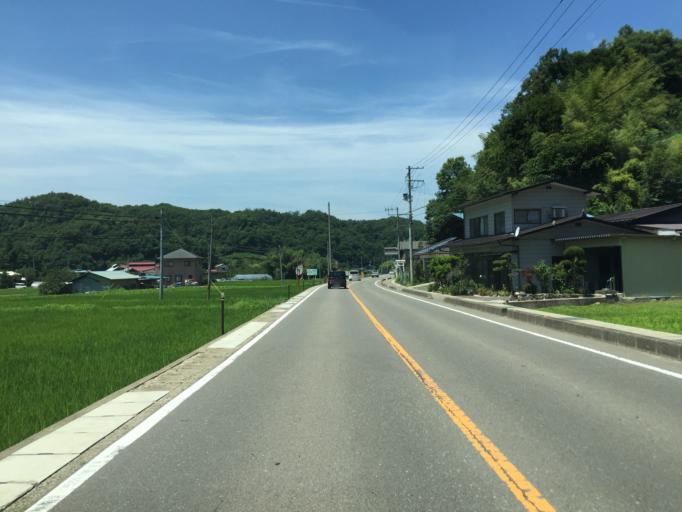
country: JP
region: Fukushima
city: Hobaramachi
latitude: 37.7652
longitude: 140.6150
